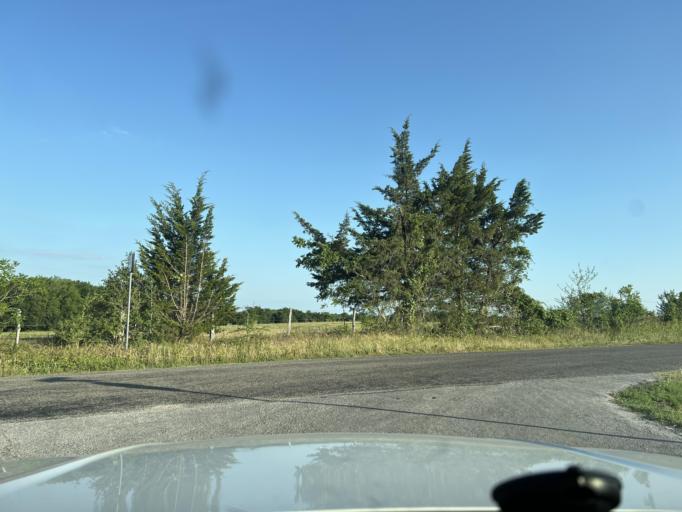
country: US
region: Texas
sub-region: Washington County
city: Brenham
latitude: 30.2108
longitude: -96.3706
